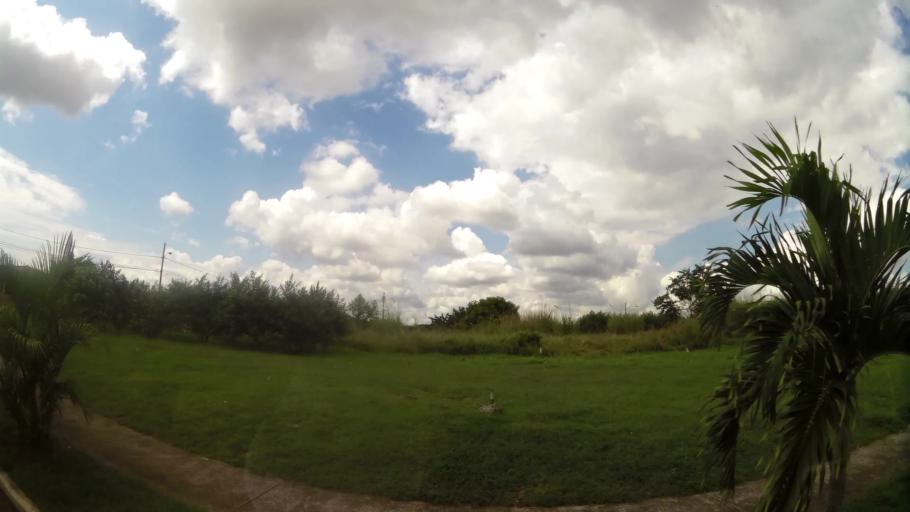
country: PA
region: Panama
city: Nuevo Arraijan
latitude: 8.9326
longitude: -79.7243
